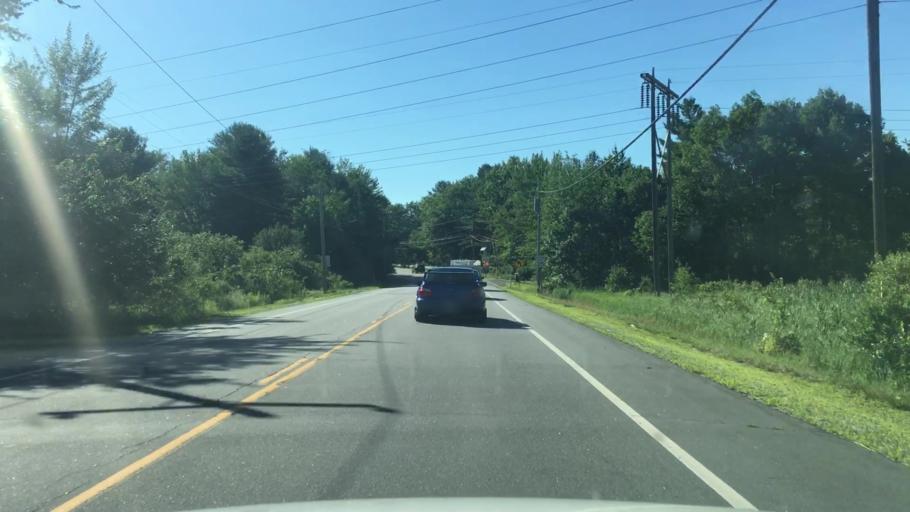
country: US
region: New Hampshire
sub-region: Rockingham County
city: Exeter
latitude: 43.0104
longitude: -71.0011
